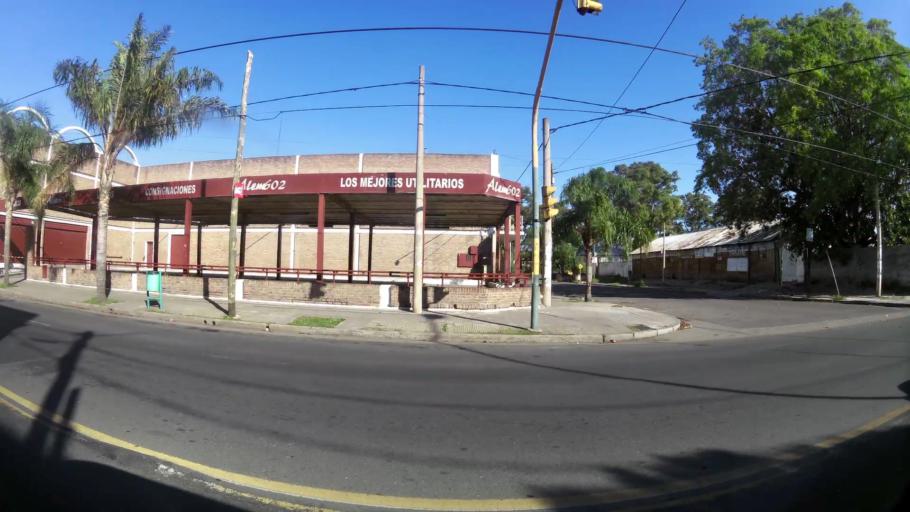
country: AR
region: Cordoba
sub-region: Departamento de Capital
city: Cordoba
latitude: -31.3951
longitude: -64.1676
